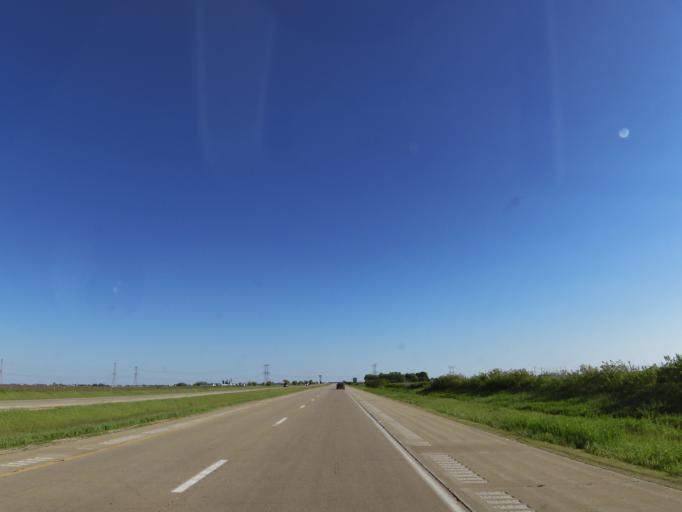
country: US
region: Illinois
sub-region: Woodford County
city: Minonk
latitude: 40.8765
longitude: -89.0369
